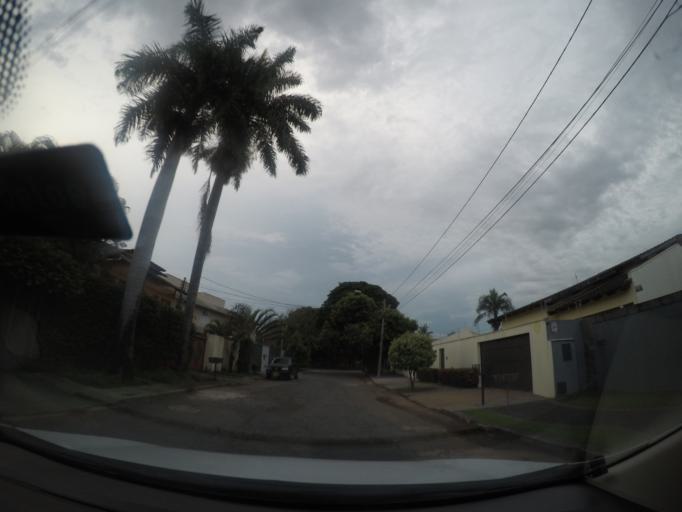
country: BR
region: Goias
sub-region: Goiania
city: Goiania
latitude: -16.6524
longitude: -49.2273
